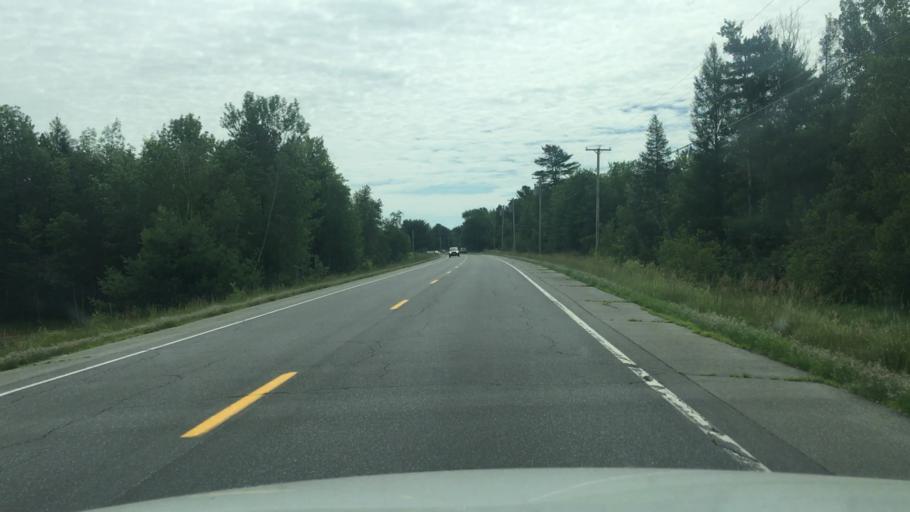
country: US
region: Maine
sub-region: Waldo County
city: Burnham
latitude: 44.6147
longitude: -69.3749
